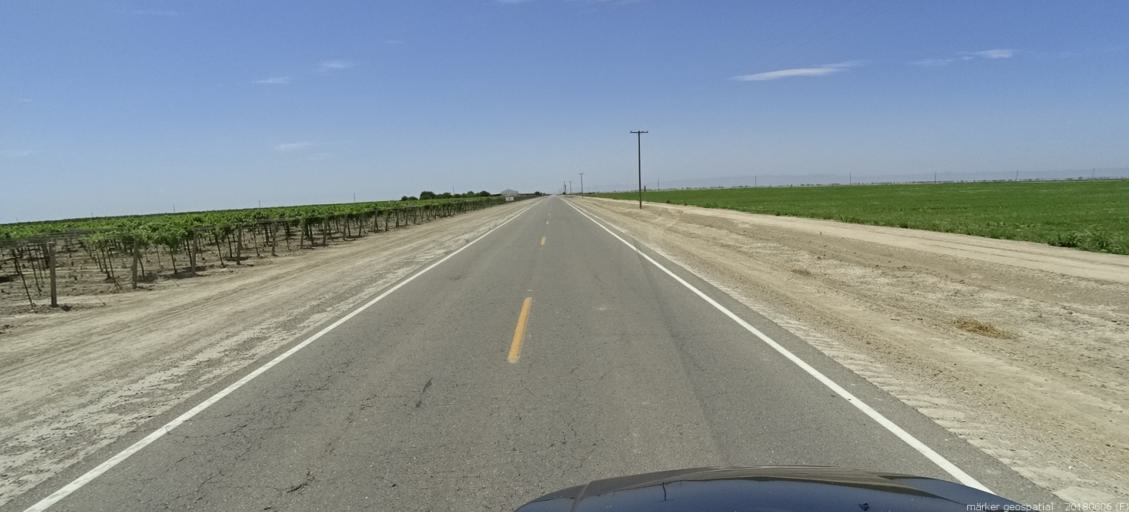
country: US
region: California
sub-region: Fresno County
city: Firebaugh
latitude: 36.9288
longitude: -120.3823
